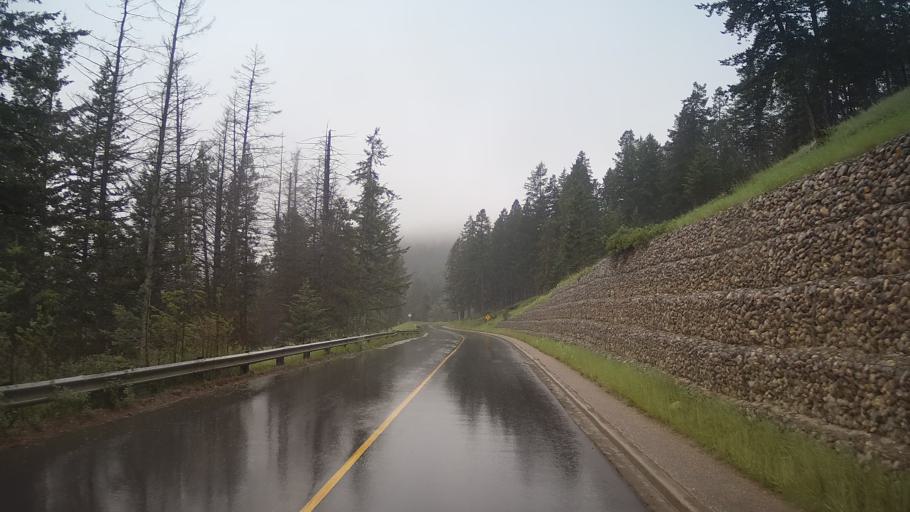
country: CA
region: Alberta
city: Jasper Park Lodge
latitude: 52.8872
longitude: -118.0821
